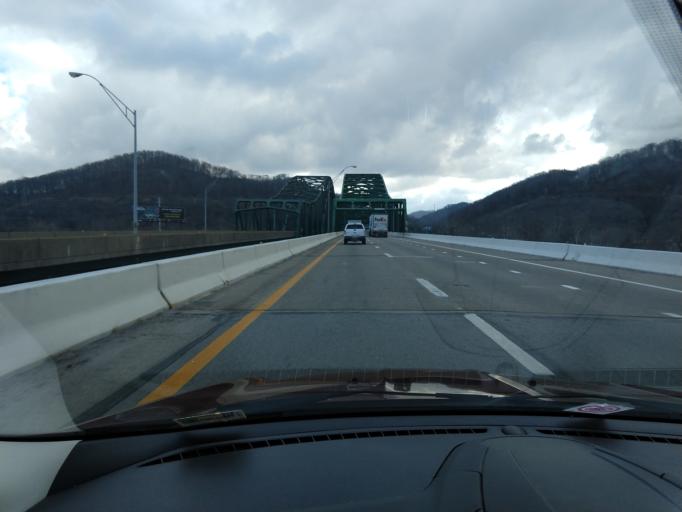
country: US
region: West Virginia
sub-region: Kanawha County
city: Rand
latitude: 38.3081
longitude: -81.5629
